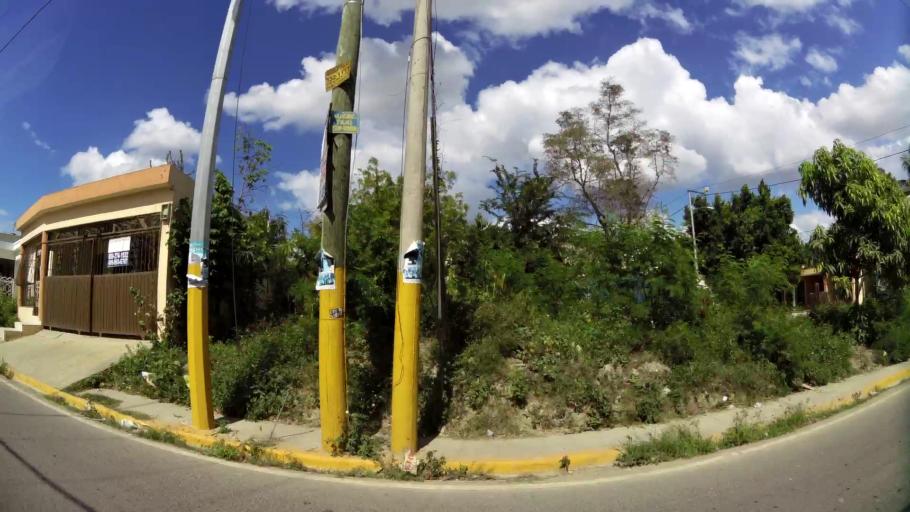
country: DO
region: Nacional
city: Ensanche Luperon
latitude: 18.5353
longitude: -69.8984
